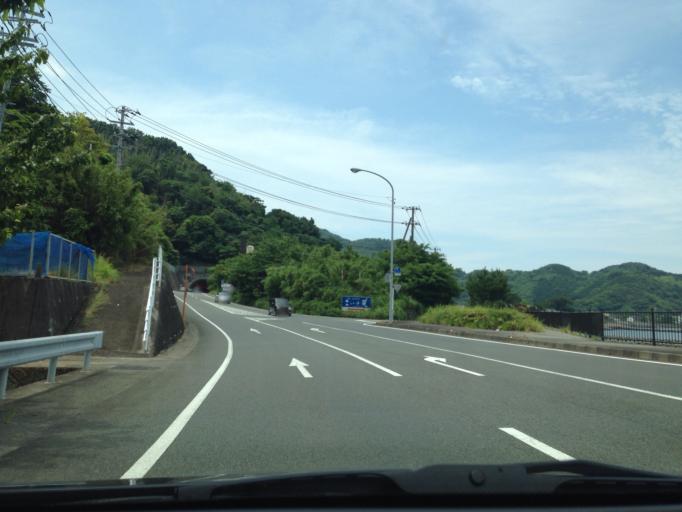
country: JP
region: Shizuoka
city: Heda
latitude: 34.8991
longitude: 138.7796
